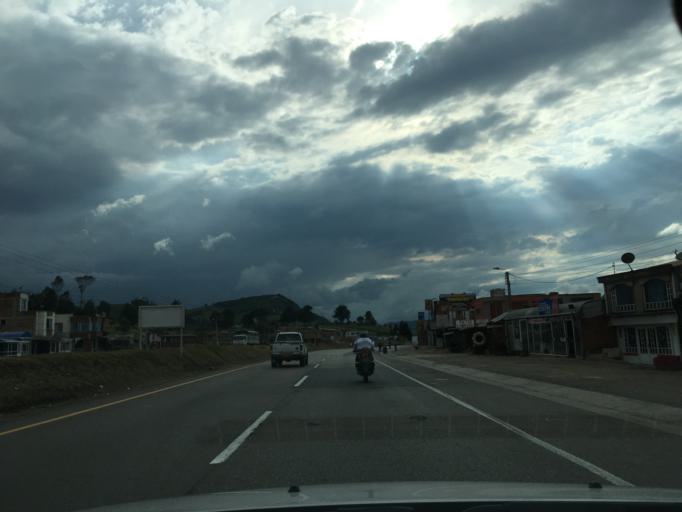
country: CO
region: Boyaca
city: Ventaquemada
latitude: 5.4164
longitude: -73.4567
